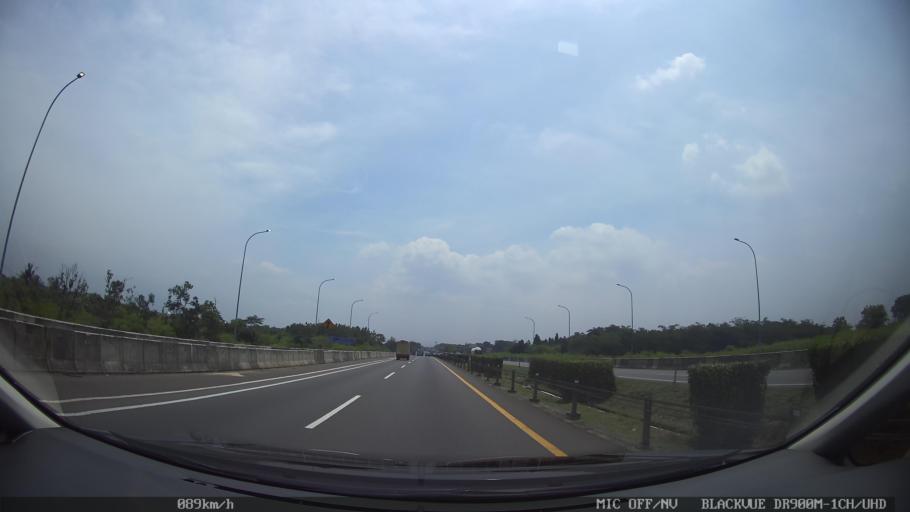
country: ID
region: Banten
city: Serang
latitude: -6.1386
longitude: 106.2421
